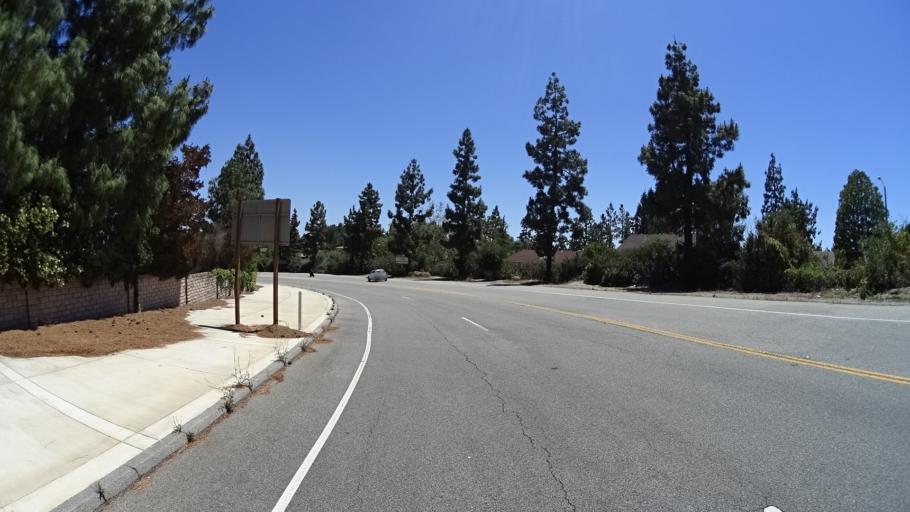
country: US
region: California
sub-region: Los Angeles County
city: La Canada Flintridge
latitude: 34.2215
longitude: -118.1930
